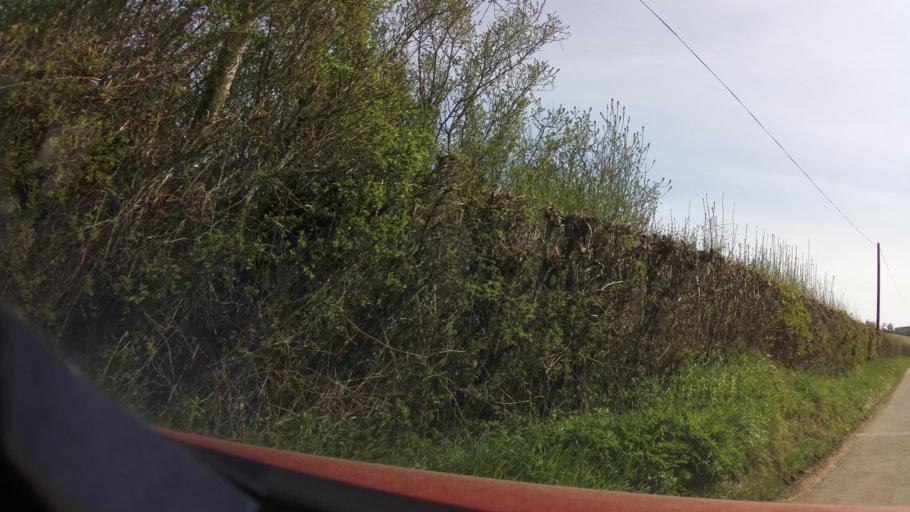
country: GB
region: England
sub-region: Dorset
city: Sherborne
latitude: 50.9986
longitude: -2.5552
